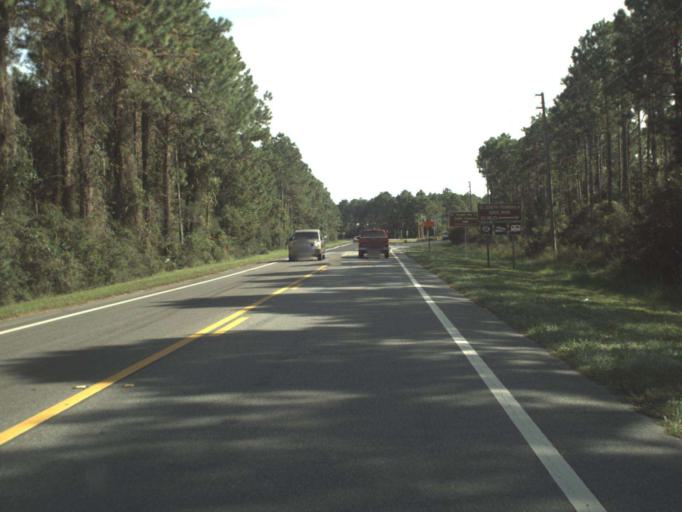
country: US
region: Florida
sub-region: Gulf County
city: Port Saint Joe
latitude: 29.7832
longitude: -85.3007
